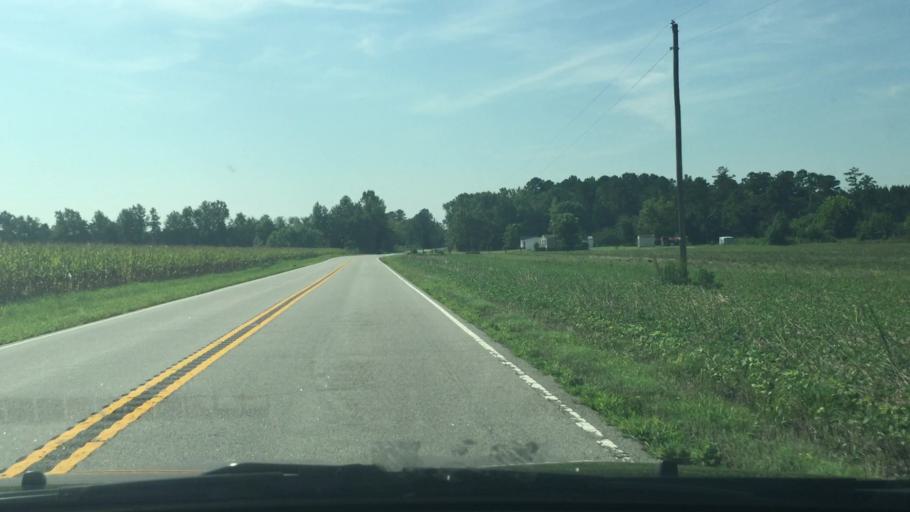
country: US
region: Virginia
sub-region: Southampton County
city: Courtland
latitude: 36.8380
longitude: -77.1294
